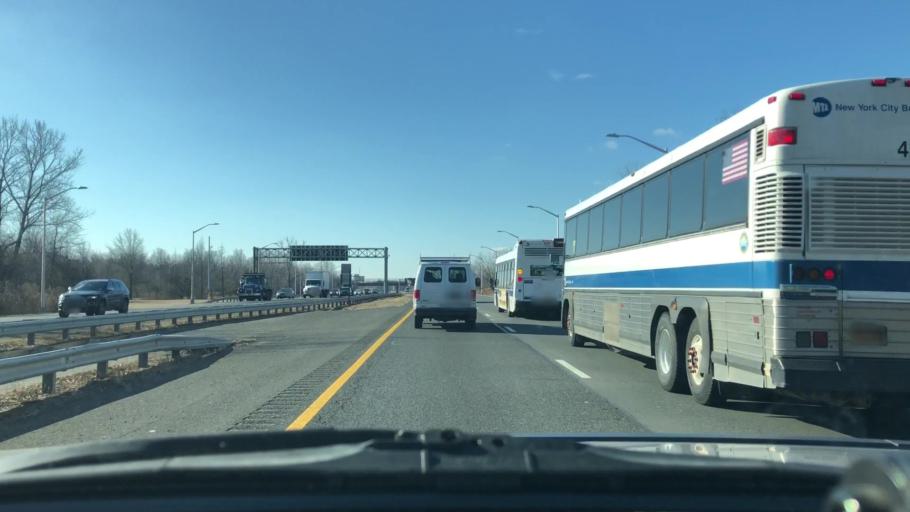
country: US
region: New York
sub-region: Richmond County
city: Bloomfield
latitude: 40.6137
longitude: -74.1797
